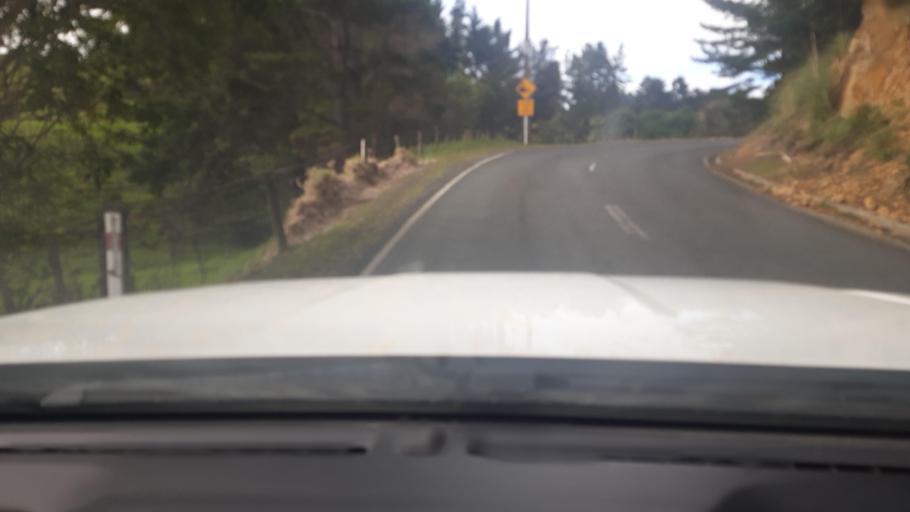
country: NZ
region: Northland
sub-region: Far North District
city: Ahipara
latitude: -35.2684
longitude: 173.2100
